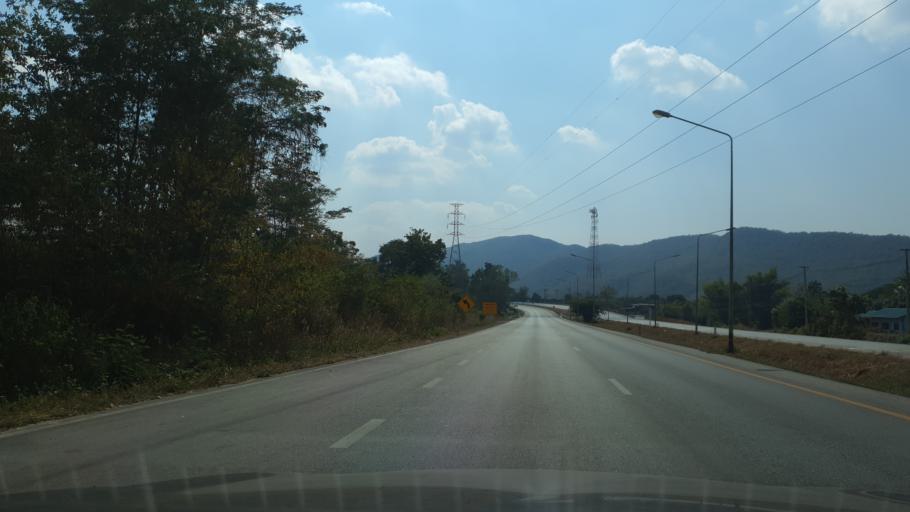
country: TH
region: Lampang
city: Mae Phrik
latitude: 17.3674
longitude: 99.1476
